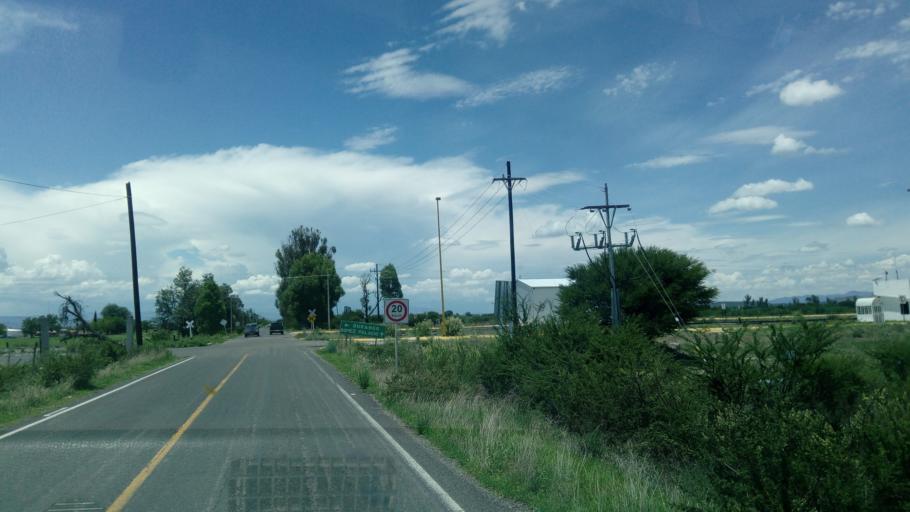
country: MX
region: Durango
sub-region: Durango
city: Jose Refugio Salcido
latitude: 24.1595
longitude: -104.5204
